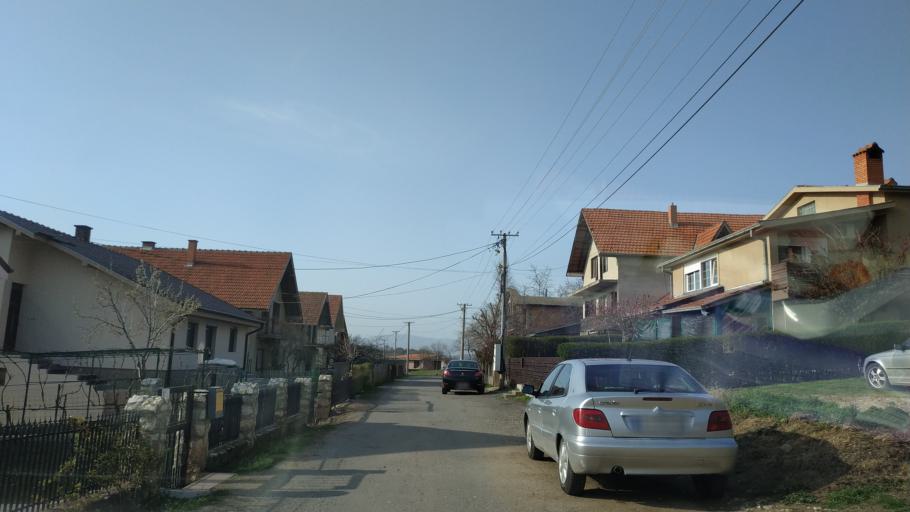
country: RS
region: Central Serbia
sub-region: Nisavski Okrug
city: Aleksinac
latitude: 43.5444
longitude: 21.7163
